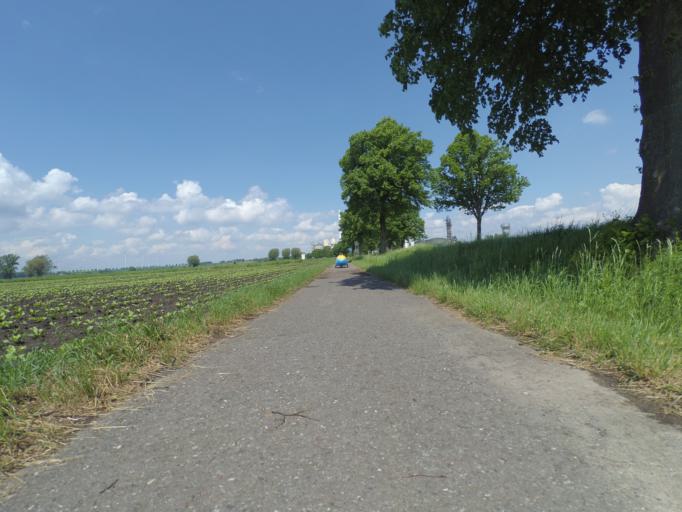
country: DE
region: Lower Saxony
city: Hohenhameln
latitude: 52.2283
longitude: 10.0340
